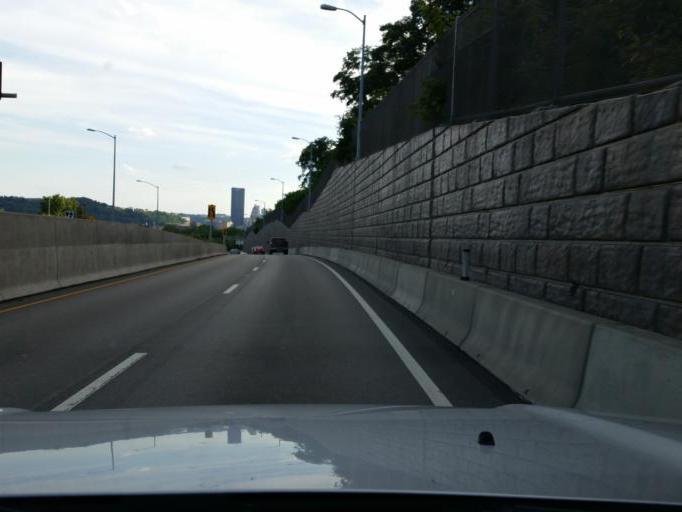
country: US
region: Pennsylvania
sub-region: Allegheny County
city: Millvale
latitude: 40.4746
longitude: -79.9716
